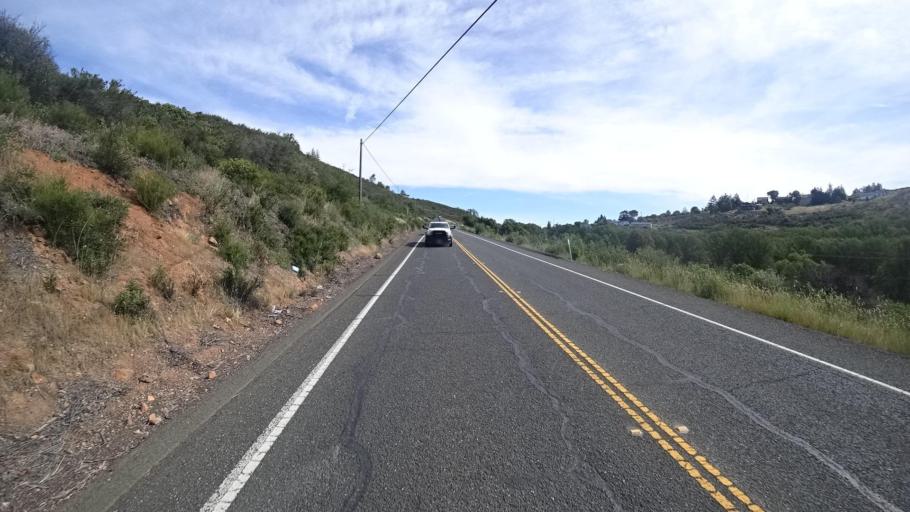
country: US
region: California
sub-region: Lake County
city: Soda Bay
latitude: 38.9465
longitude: -122.7348
